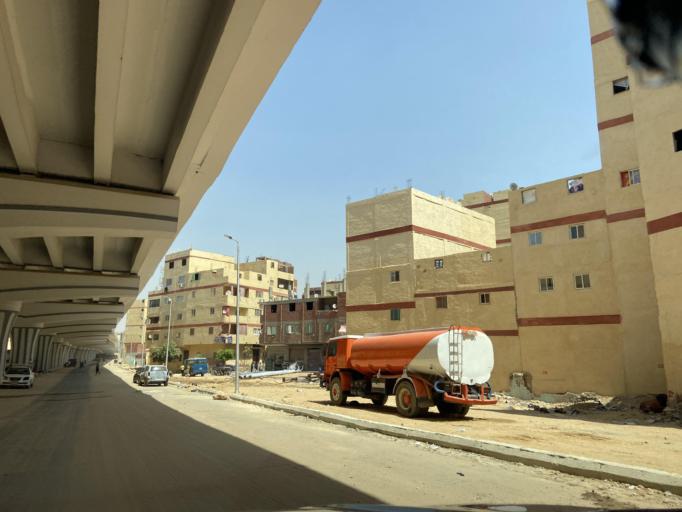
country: EG
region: Muhafazat al Qahirah
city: Cairo
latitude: 30.0680
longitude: 31.3838
